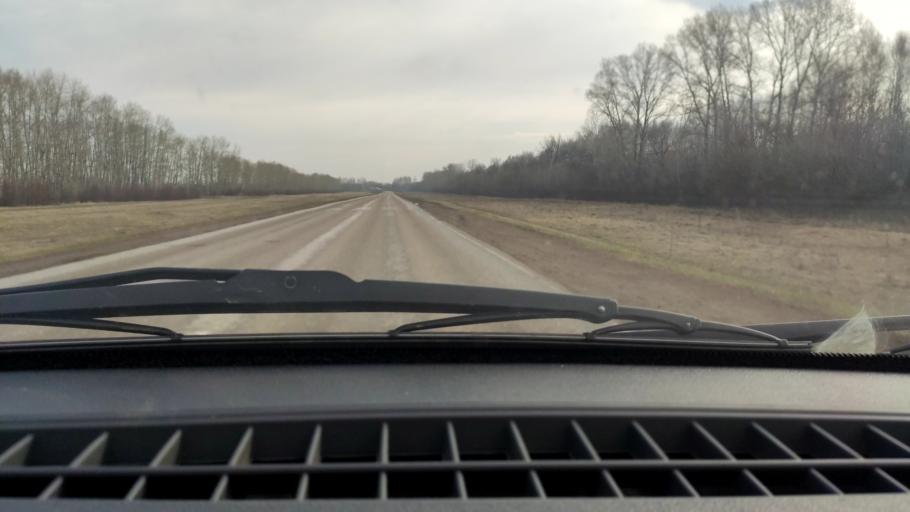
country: RU
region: Bashkortostan
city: Davlekanovo
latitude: 54.3553
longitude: 55.1860
